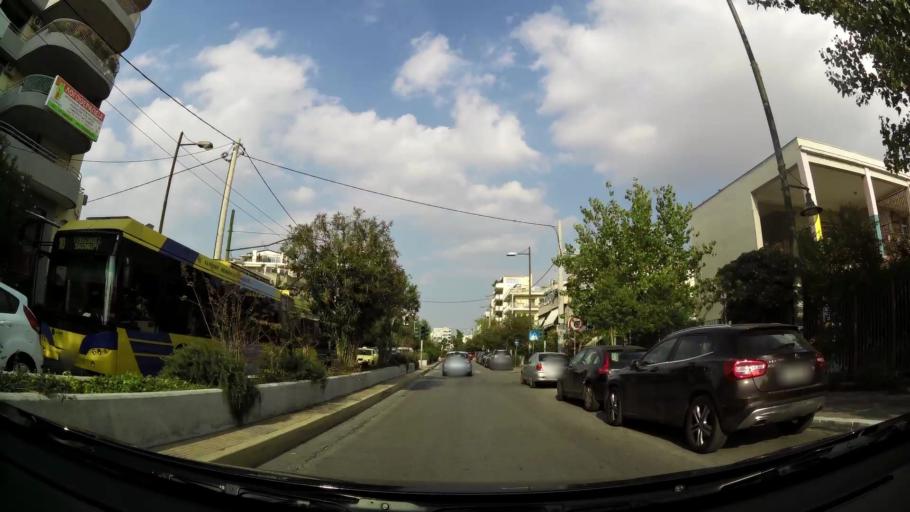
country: GR
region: Attica
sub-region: Nomarchia Athinas
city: Moskhaton
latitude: 37.9414
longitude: 23.6880
